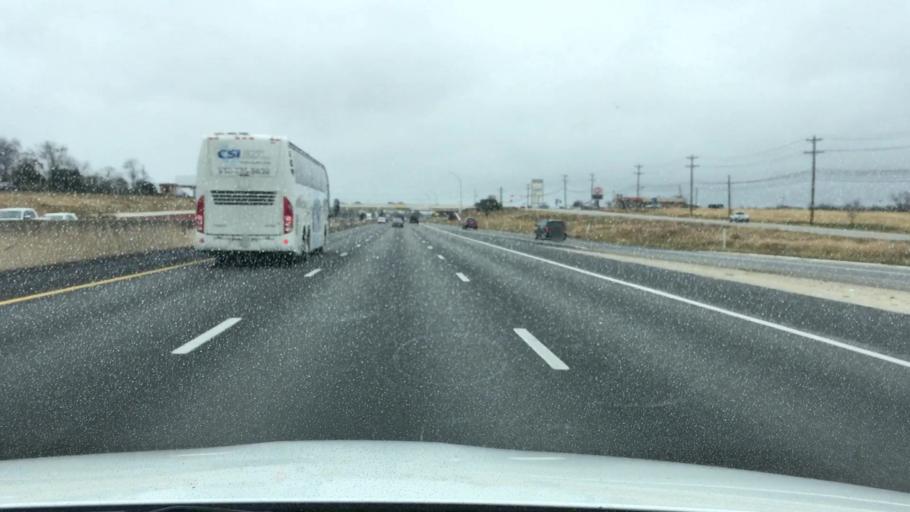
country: US
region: Texas
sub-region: Hays County
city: Kyle
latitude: 29.9846
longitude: -97.8730
